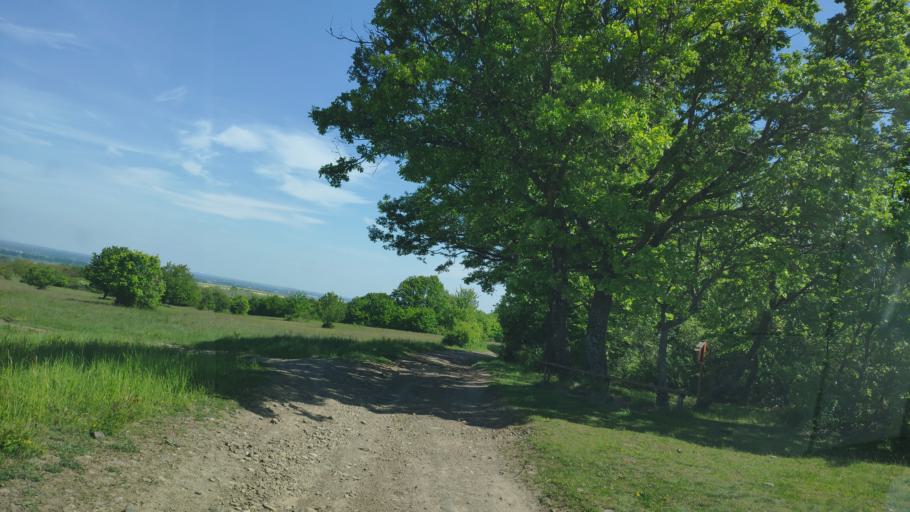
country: SK
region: Kosicky
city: Secovce
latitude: 48.6982
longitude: 21.5946
